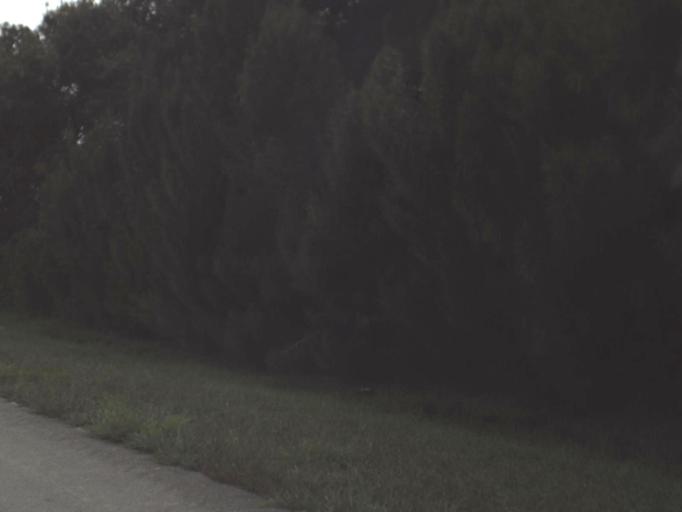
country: US
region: Florida
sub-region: DeSoto County
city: Southeast Arcadia
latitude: 27.1631
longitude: -81.8191
